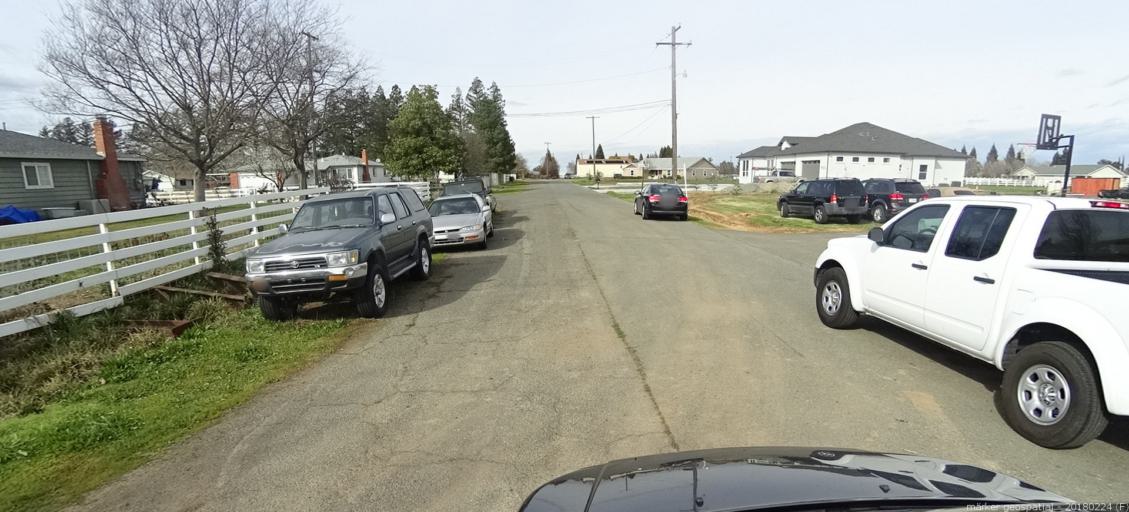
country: US
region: California
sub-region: Sacramento County
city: Elverta
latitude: 38.7113
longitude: -121.4482
